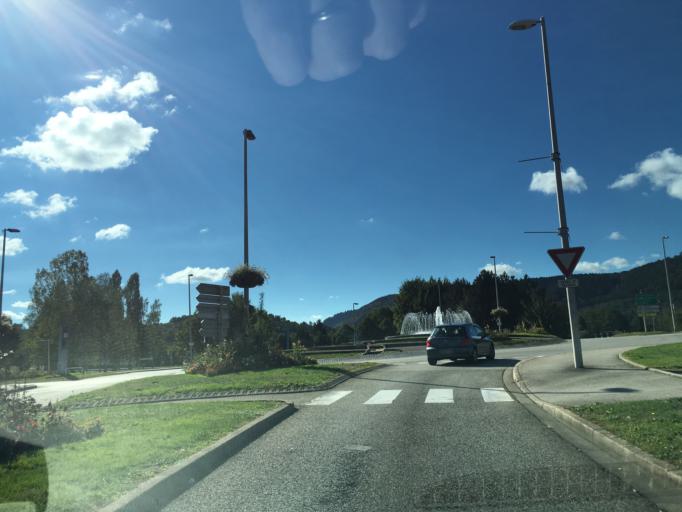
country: FR
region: Lorraine
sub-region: Departement des Vosges
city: Saint-Die-des-Vosges
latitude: 48.2921
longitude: 6.9328
